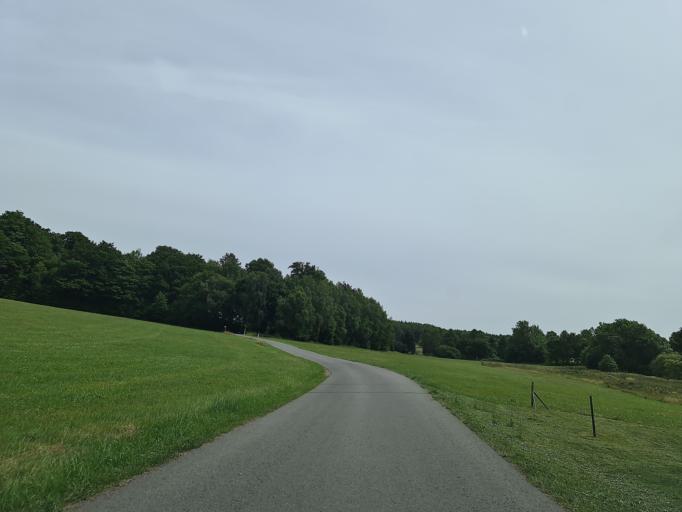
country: DE
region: Saxony
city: Neuhausen
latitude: 50.6826
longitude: 13.4818
